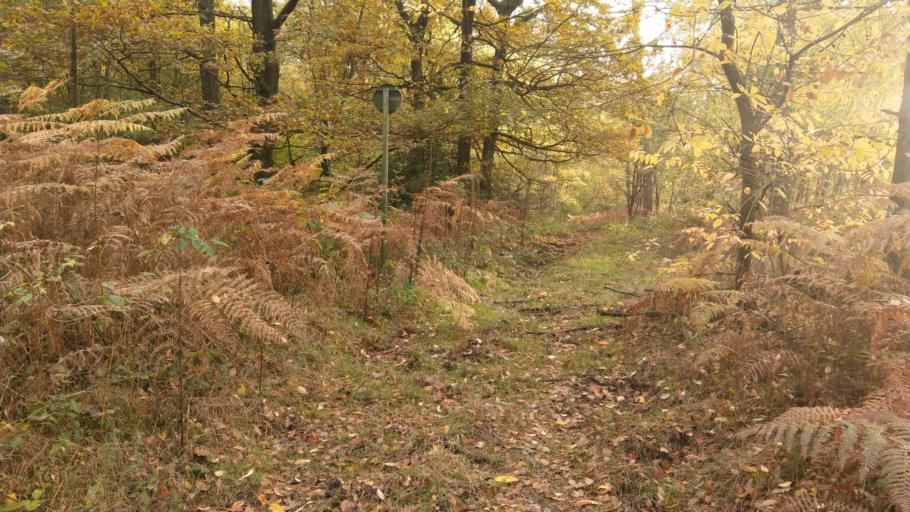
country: BE
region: Wallonia
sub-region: Province de Liege
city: La Calamine
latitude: 50.7322
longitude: 6.0242
